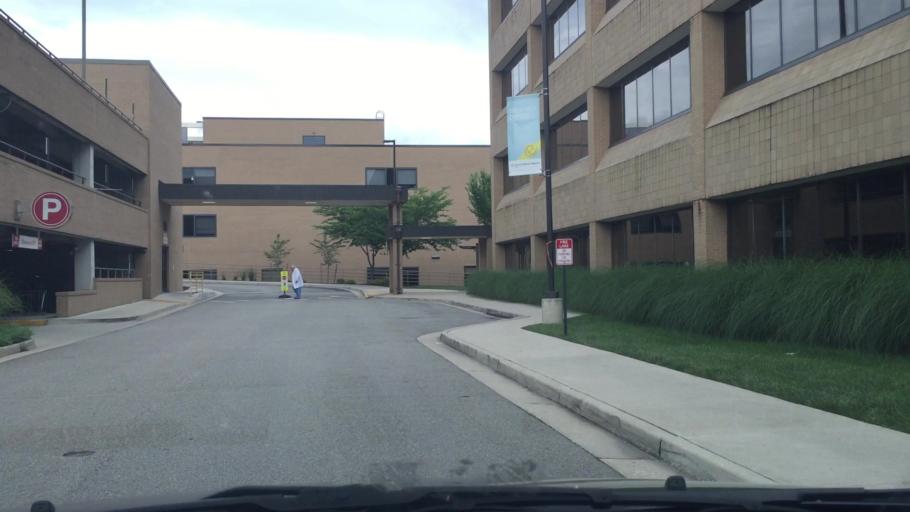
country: US
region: Virginia
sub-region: Henrico County
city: Tuckahoe
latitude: 37.6042
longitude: -77.5417
